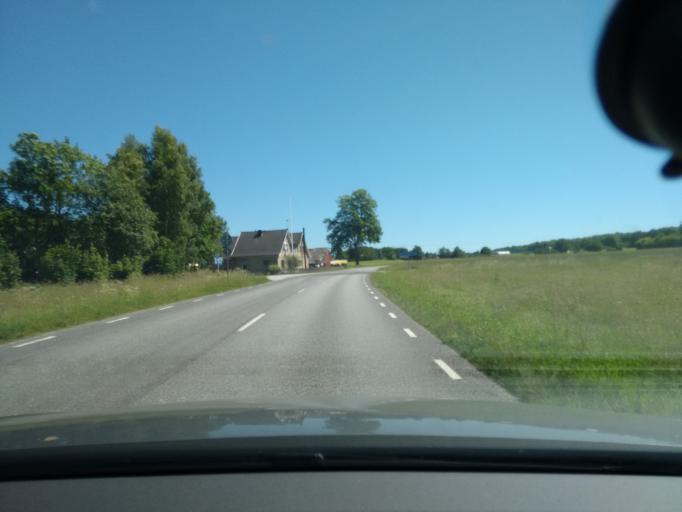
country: SE
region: Skane
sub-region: Horby Kommun
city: Hoerby
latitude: 55.8027
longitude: 13.7454
